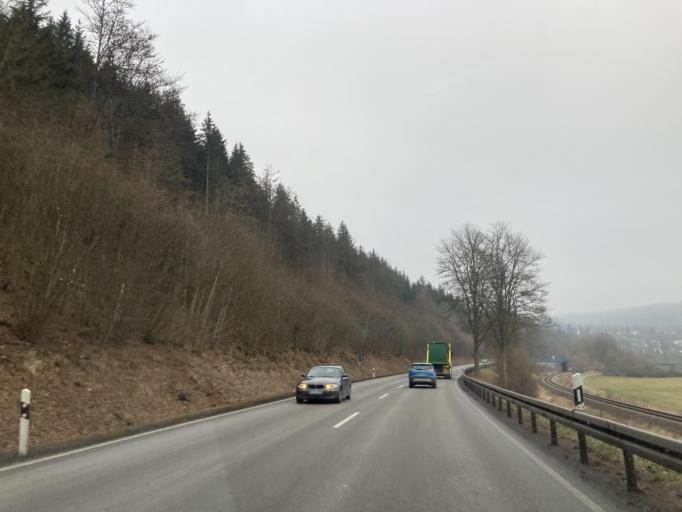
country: DE
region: Baden-Wuerttemberg
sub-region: Freiburg Region
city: Immendingen
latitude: 47.9476
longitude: 8.7560
